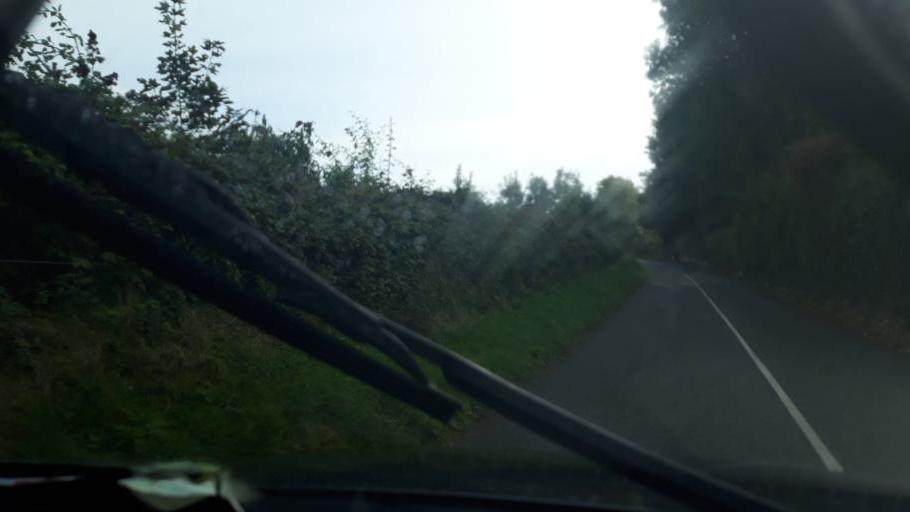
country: IE
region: Leinster
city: Sandyford
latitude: 53.2496
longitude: -6.2181
